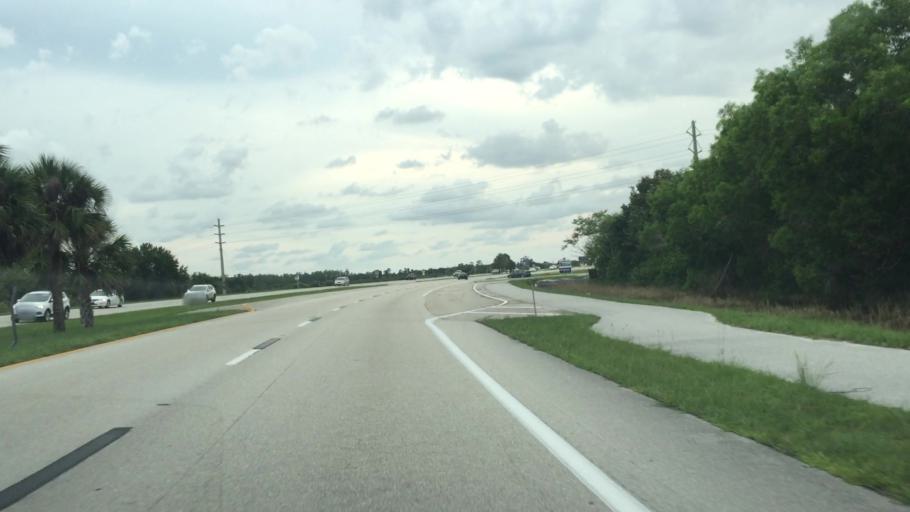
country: US
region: Florida
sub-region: Lee County
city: Villas
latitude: 26.5304
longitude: -81.8456
